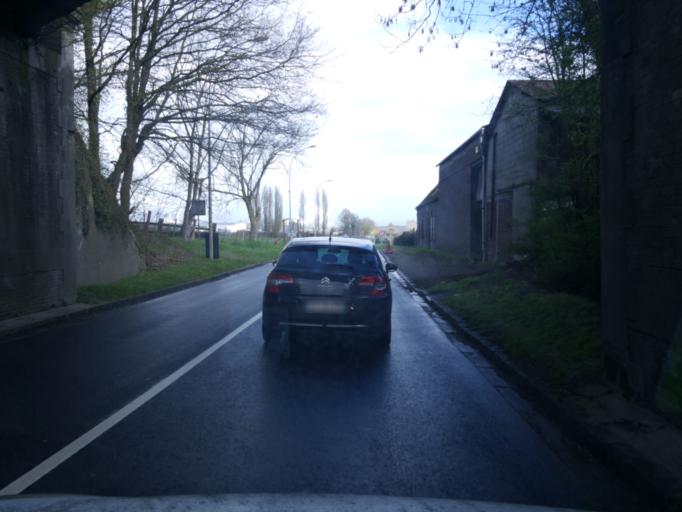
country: FR
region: Picardie
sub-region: Departement de l'Oise
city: Auneuil
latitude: 49.3774
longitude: 1.9928
